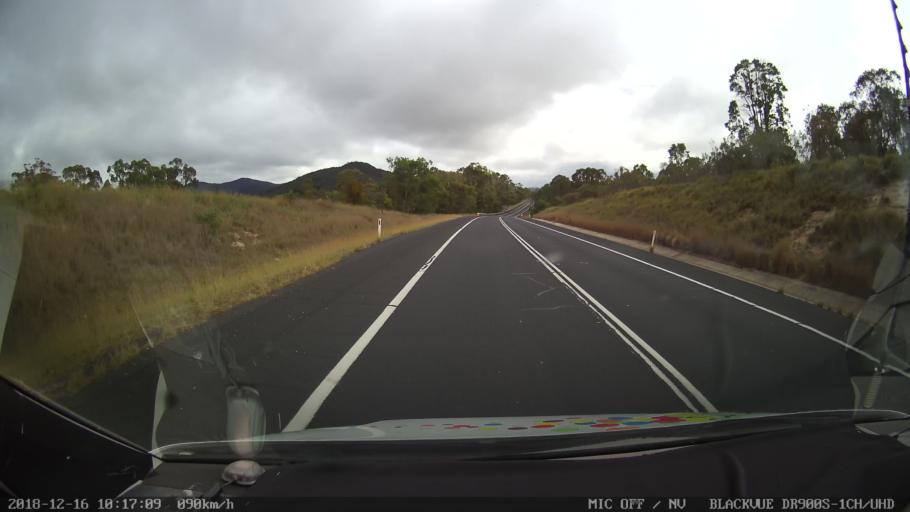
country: AU
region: New South Wales
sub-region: Tenterfield Municipality
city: Carrolls Creek
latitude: -29.2591
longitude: 151.9892
